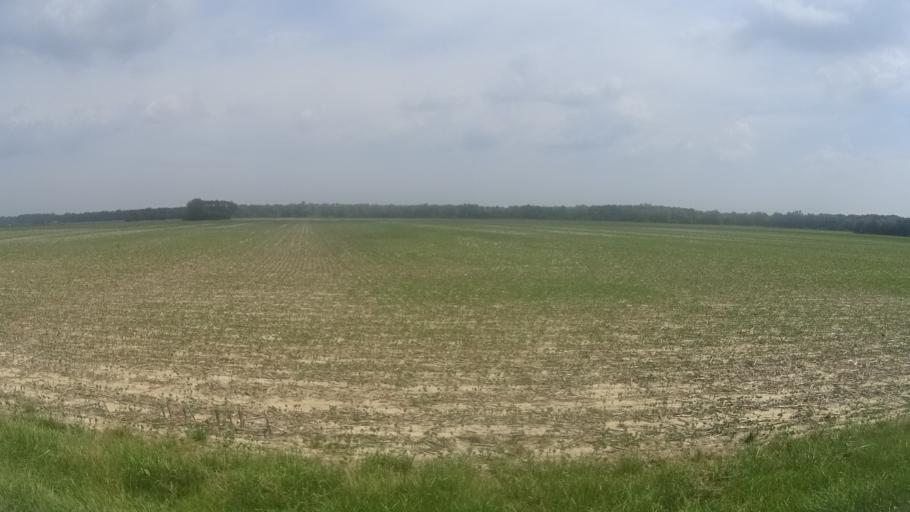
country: US
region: Ohio
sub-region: Erie County
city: Milan
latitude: 41.3463
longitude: -82.6840
